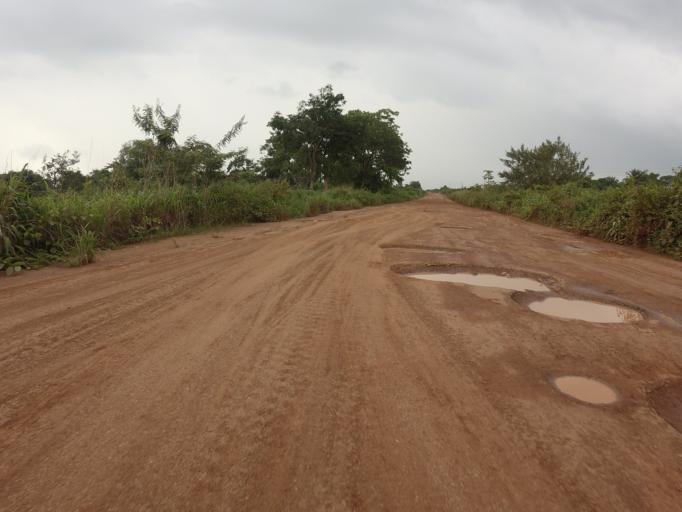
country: GH
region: Volta
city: Kpandu
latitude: 7.0137
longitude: 0.4283
